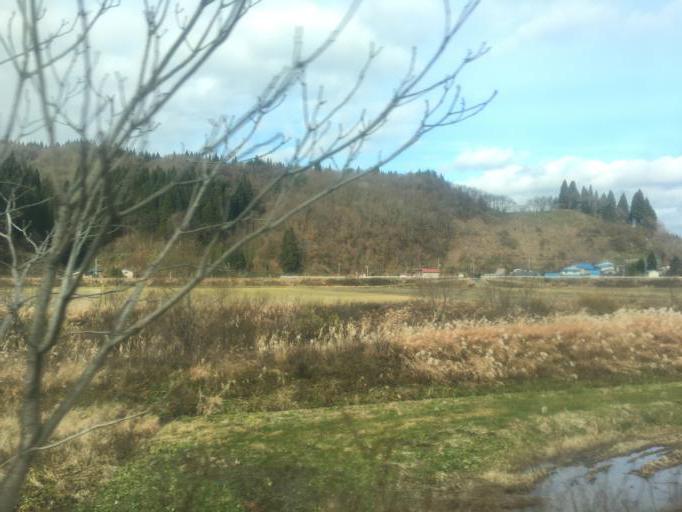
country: JP
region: Akita
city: Takanosu
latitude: 40.2167
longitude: 140.3165
